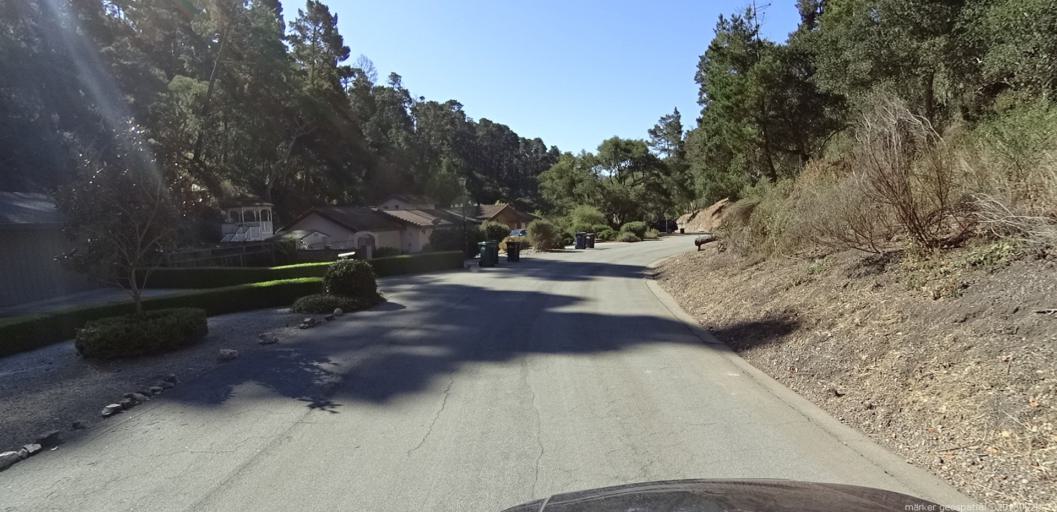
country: US
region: California
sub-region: Monterey County
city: Carmel-by-the-Sea
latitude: 36.5536
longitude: -121.8950
